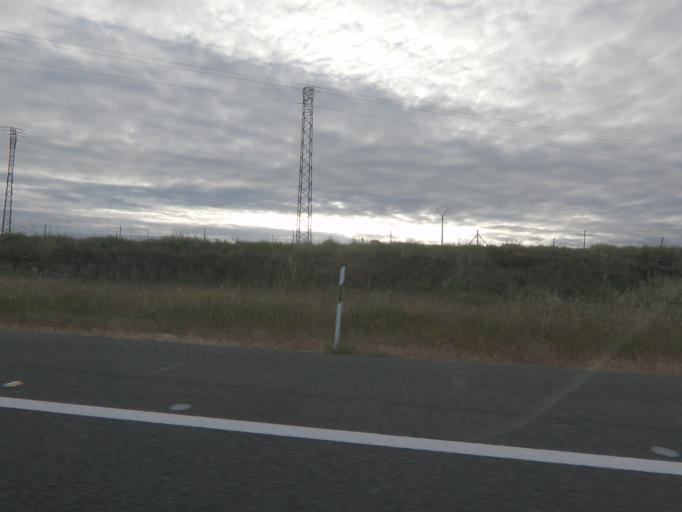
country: ES
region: Extremadura
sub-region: Provincia de Caceres
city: Casar de Caceres
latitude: 39.5504
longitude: -6.4034
